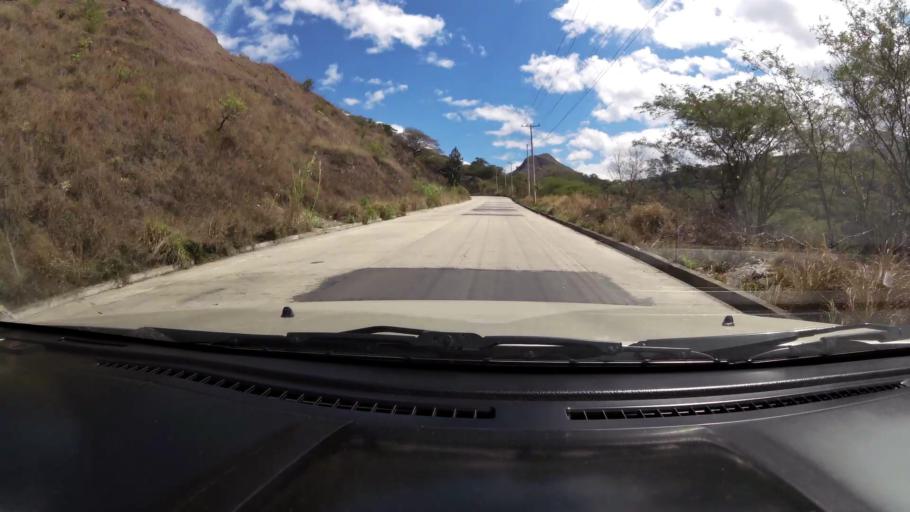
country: EC
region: Azuay
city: Cuenca
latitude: -3.2234
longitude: -79.2048
